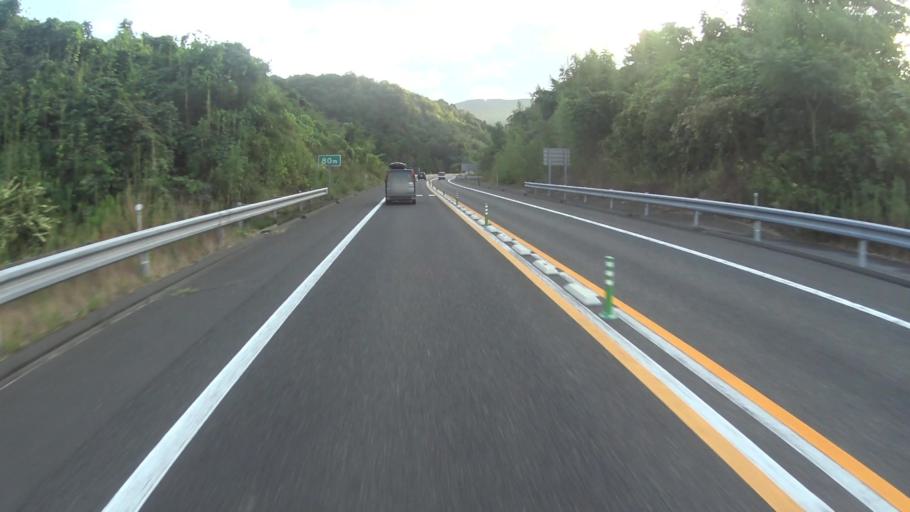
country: JP
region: Kyoto
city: Miyazu
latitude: 35.5030
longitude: 135.1811
